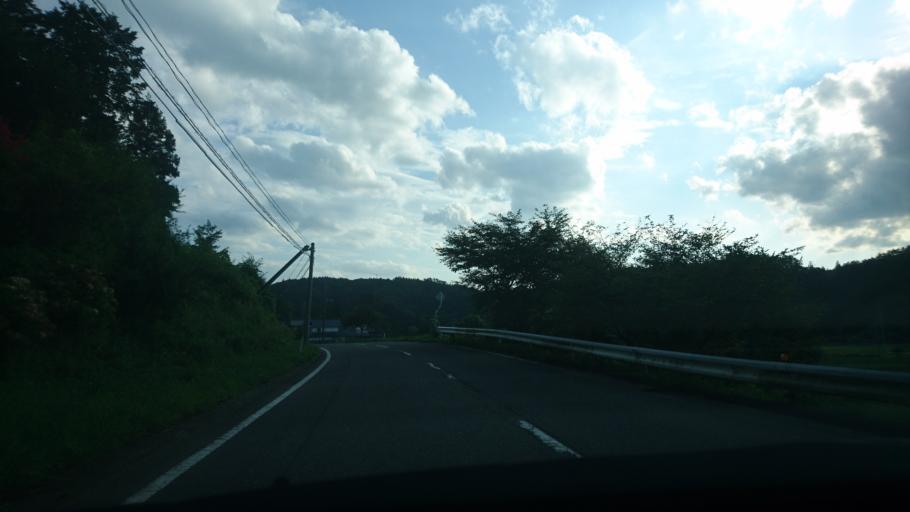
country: JP
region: Iwate
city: Ichinoseki
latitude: 39.0217
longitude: 141.2910
